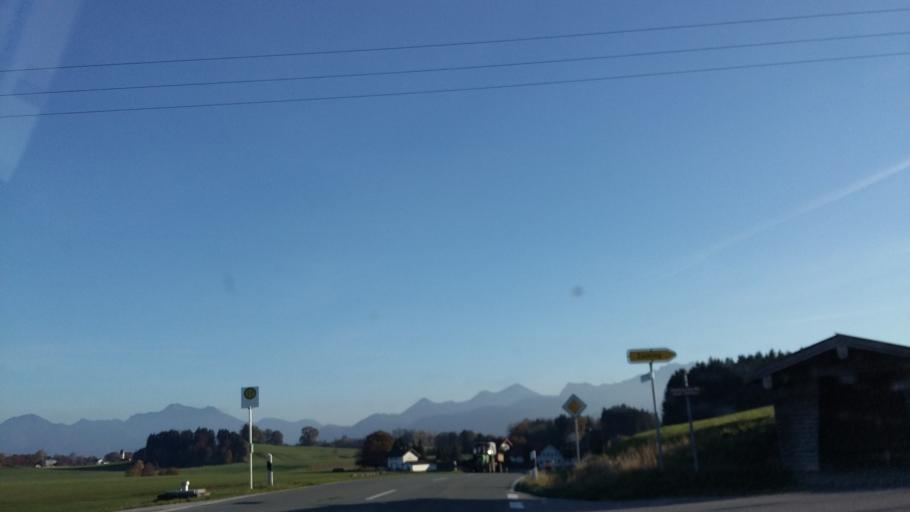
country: DE
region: Bavaria
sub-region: Upper Bavaria
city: Rimsting
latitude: 47.8615
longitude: 12.3162
